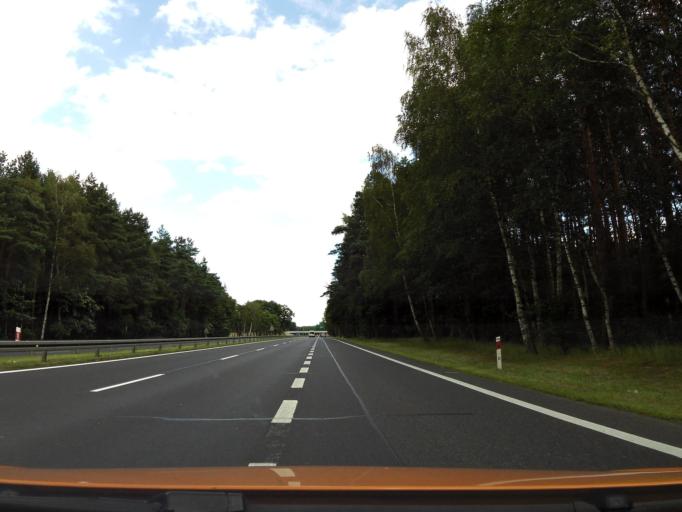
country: PL
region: West Pomeranian Voivodeship
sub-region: Powiat goleniowski
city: Goleniow
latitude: 53.5840
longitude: 14.8150
